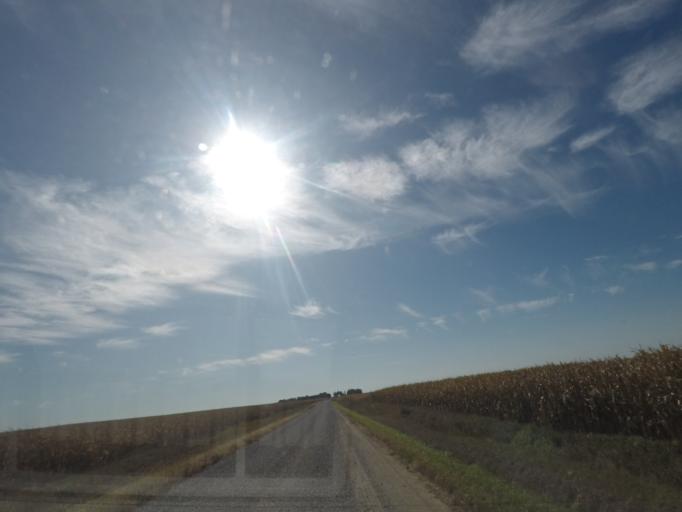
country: US
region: Iowa
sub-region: Story County
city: Nevada
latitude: 42.0614
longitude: -93.3293
